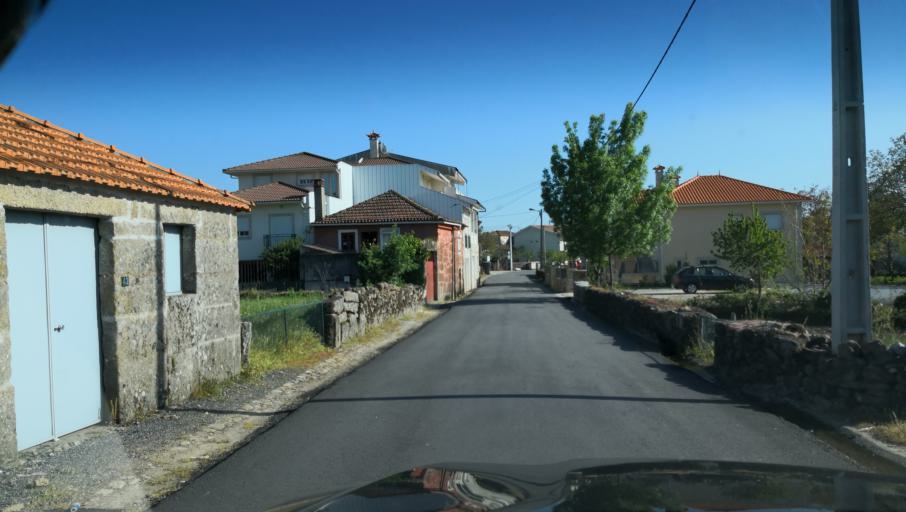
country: PT
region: Vila Real
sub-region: Vila Real
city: Vila Real
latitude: 41.2839
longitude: -7.6835
